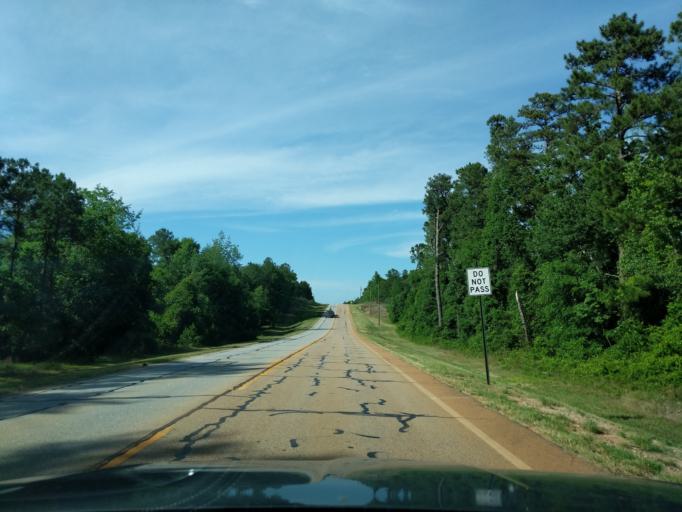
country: US
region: Georgia
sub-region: Jefferson County
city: Wrens
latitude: 33.2919
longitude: -82.3793
